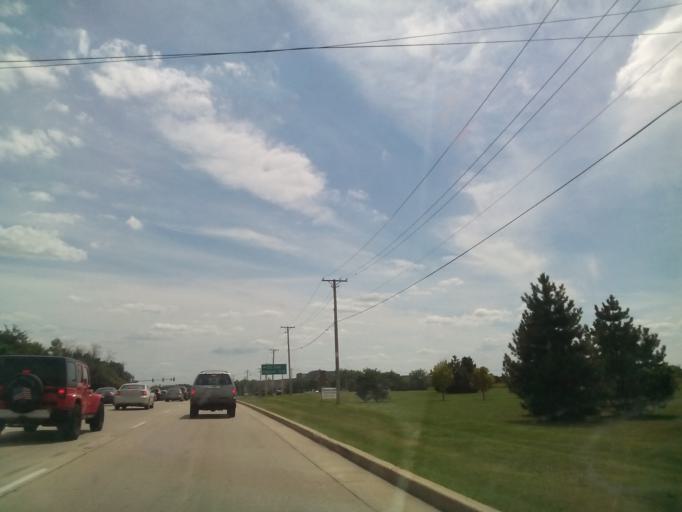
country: US
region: Illinois
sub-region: DuPage County
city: Naperville
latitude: 41.7350
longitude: -88.2063
